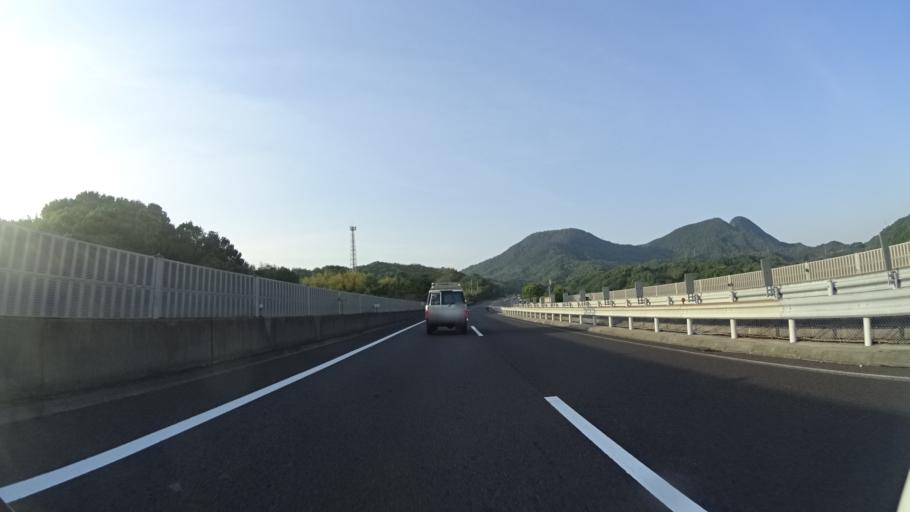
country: JP
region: Kagawa
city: Tadotsu
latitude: 34.1938
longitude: 133.7317
